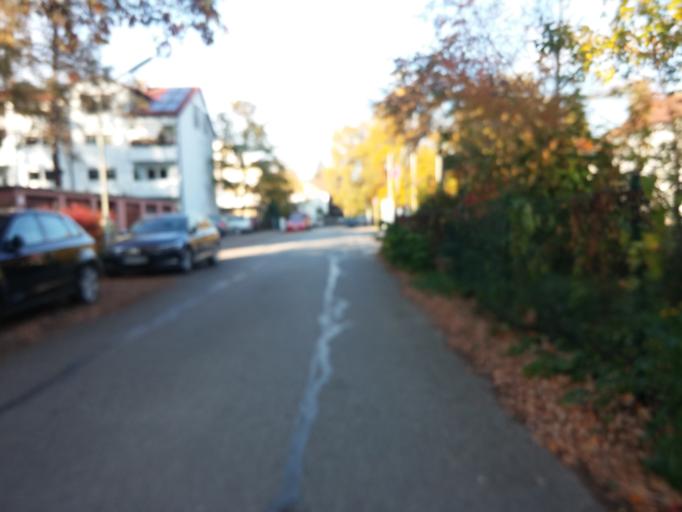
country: DE
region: Bavaria
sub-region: Upper Bavaria
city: Vaterstetten
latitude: 48.0967
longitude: 11.7758
